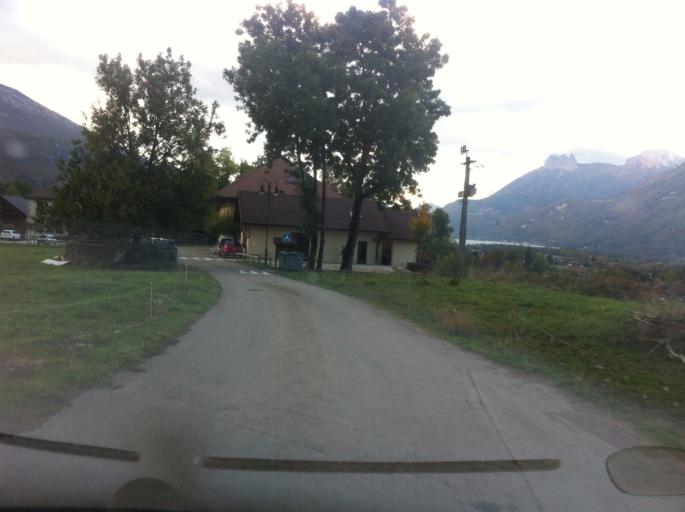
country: FR
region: Rhone-Alpes
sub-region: Departement de la Haute-Savoie
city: Doussard
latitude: 45.7635
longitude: 6.2198
